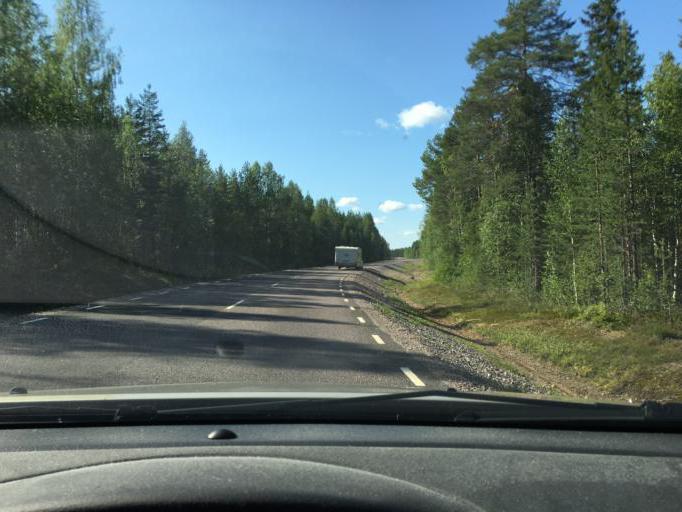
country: SE
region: Norrbotten
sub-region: Lulea Kommun
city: Ranea
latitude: 66.0483
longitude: 22.2364
